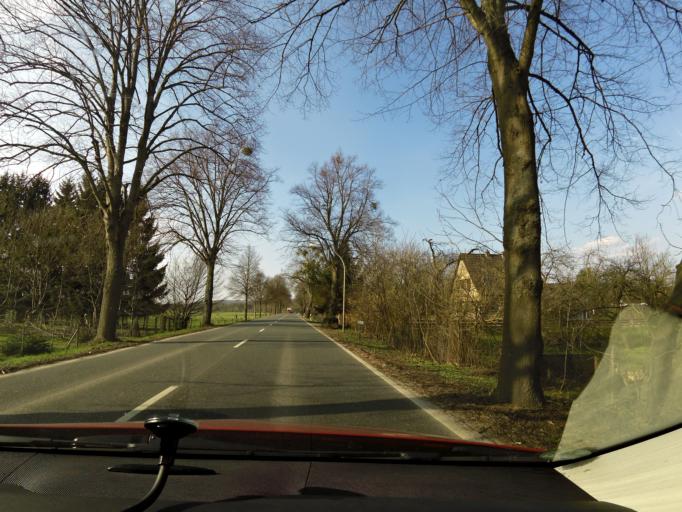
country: DE
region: Lower Saxony
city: Gieboldehausen
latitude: 51.6111
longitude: 10.2107
